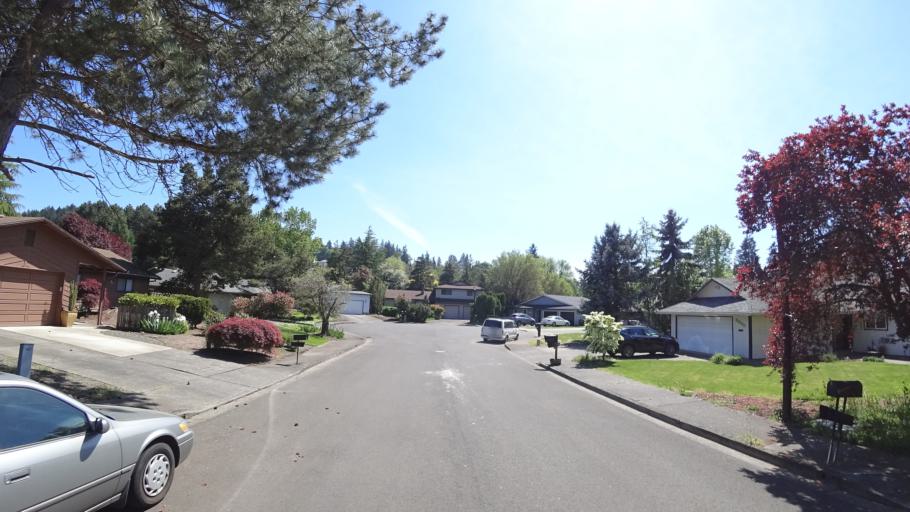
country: US
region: Oregon
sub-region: Washington County
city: Aloha
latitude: 45.4779
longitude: -122.8483
